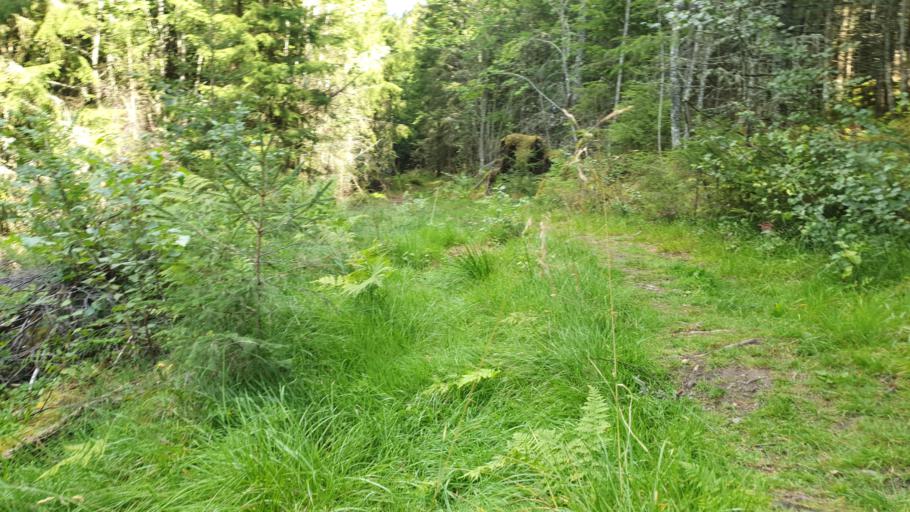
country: NO
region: Nord-Trondelag
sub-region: Levanger
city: Levanger
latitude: 63.7712
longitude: 11.3746
